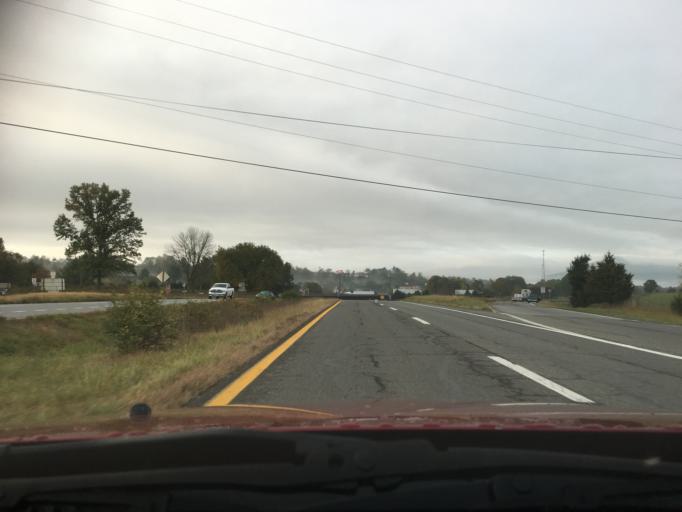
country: US
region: Virginia
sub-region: Pulaski County
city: Dublin
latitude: 37.0818
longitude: -80.6909
